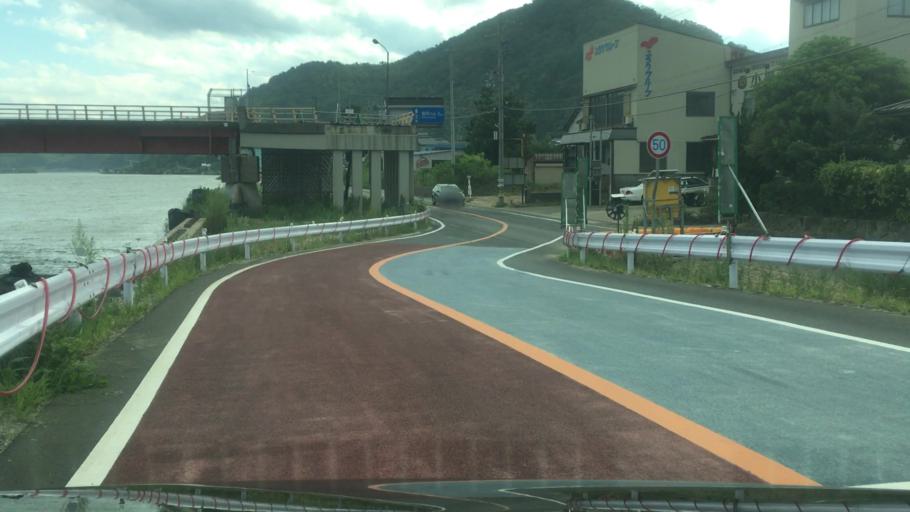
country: JP
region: Hyogo
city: Toyooka
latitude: 35.6083
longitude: 134.8037
